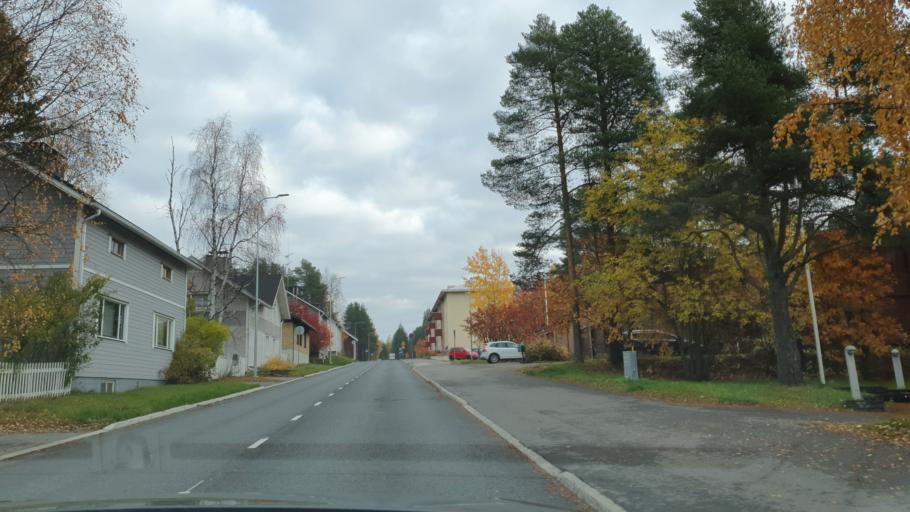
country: FI
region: Lapland
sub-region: Rovaniemi
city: Rovaniemi
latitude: 66.4961
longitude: 25.7449
